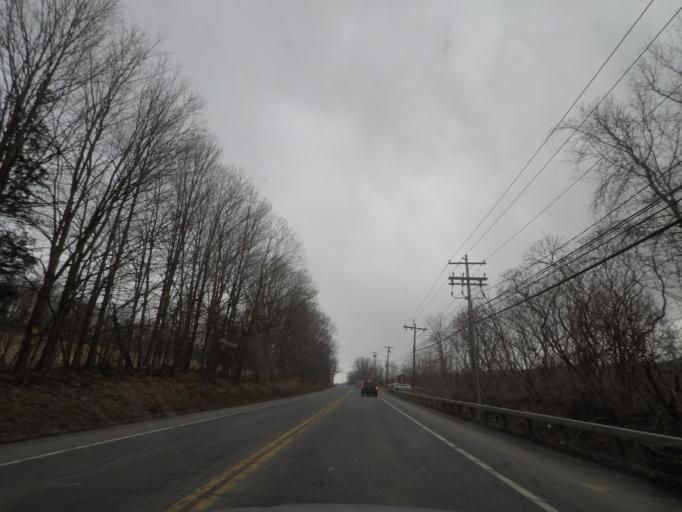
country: US
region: New York
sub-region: Onondaga County
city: Fayetteville
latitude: 43.0344
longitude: -75.9788
